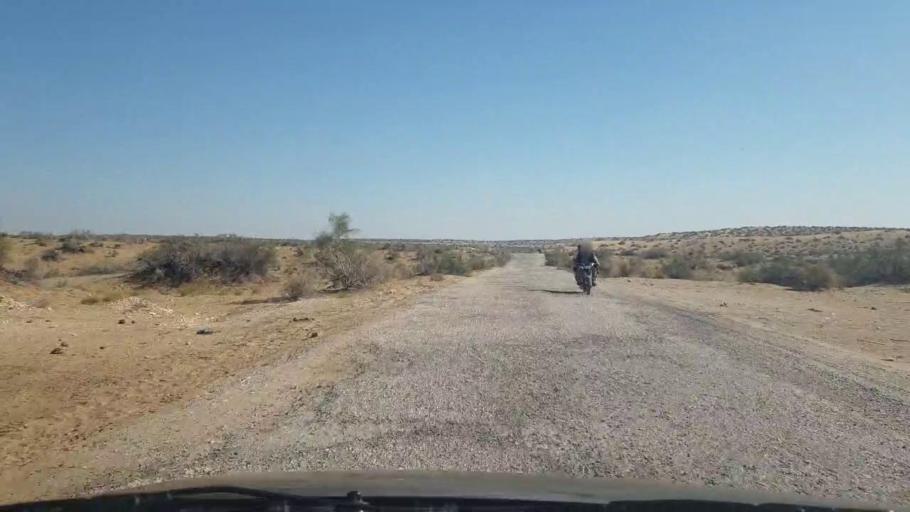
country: PK
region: Sindh
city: Bozdar
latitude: 27.0029
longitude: 68.8419
